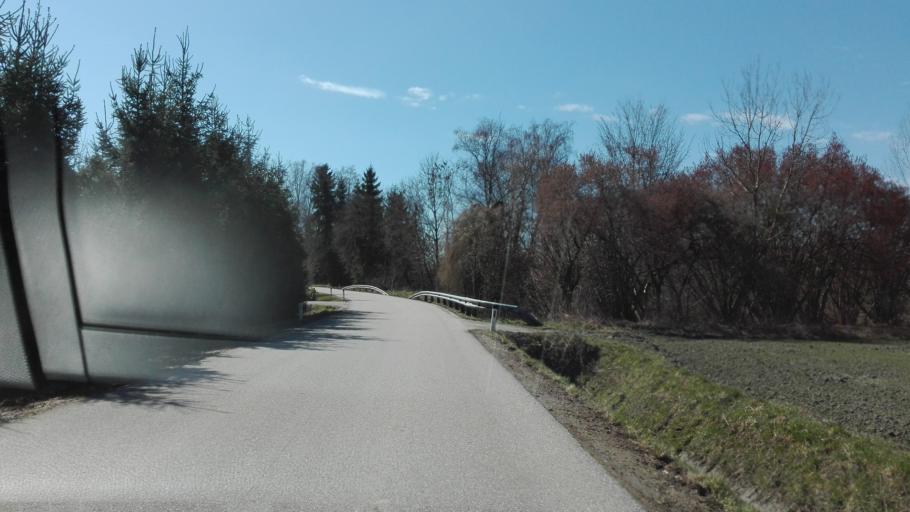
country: AT
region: Upper Austria
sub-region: Wels-Land
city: Buchkirchen
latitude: 48.2367
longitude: 13.9726
